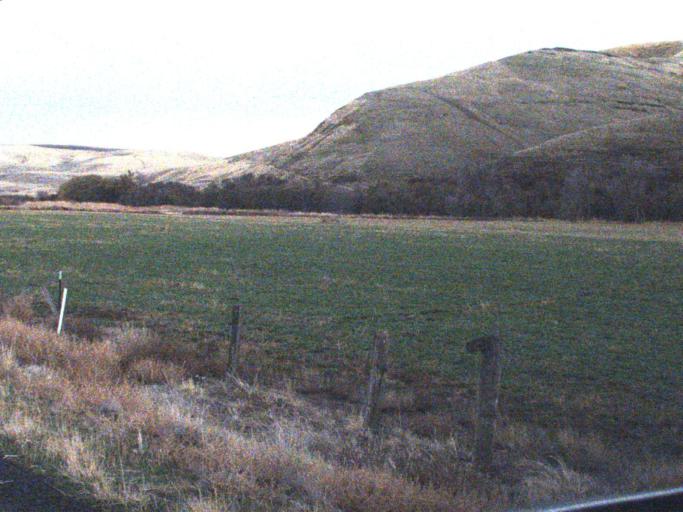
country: US
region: Washington
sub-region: Columbia County
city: Dayton
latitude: 46.5084
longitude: -118.0820
